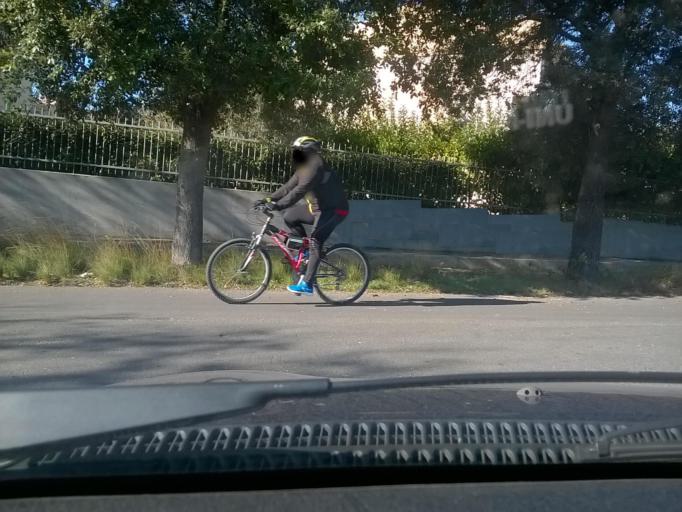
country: IT
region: Apulia
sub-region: Provincia di Taranto
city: Paolo VI
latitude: 40.5184
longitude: 17.2836
